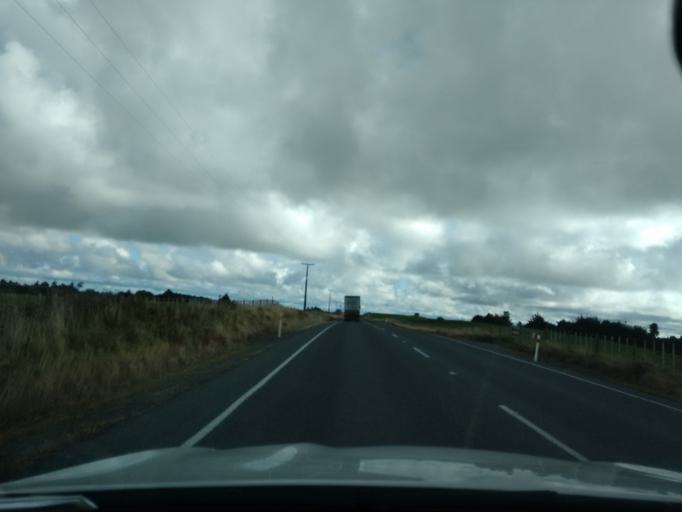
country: NZ
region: Manawatu-Wanganui
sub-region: Ruapehu District
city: Waiouru
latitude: -39.3524
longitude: 175.3589
